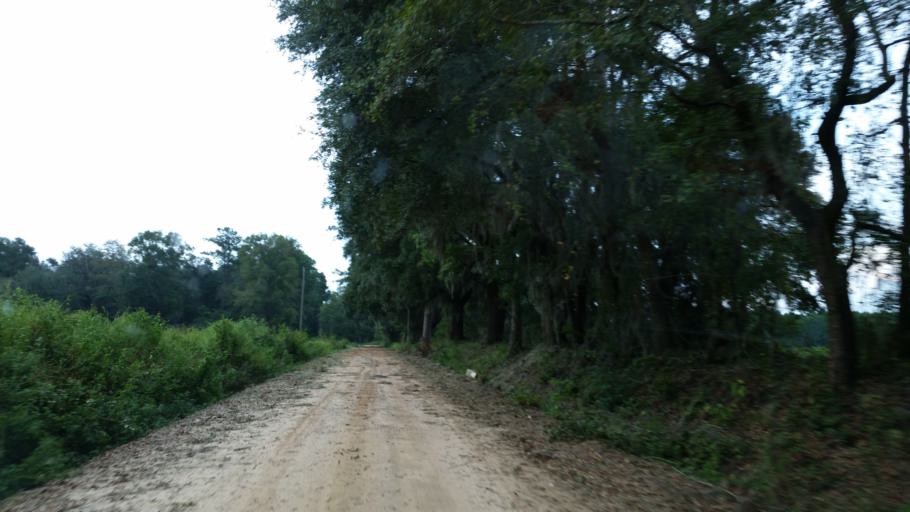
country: US
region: Georgia
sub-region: Lowndes County
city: Valdosta
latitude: 30.7210
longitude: -83.2883
